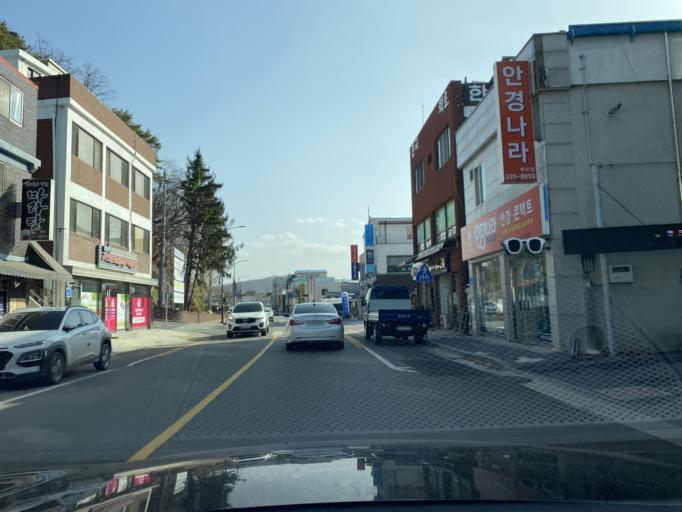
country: KR
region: Chungcheongnam-do
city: Yesan
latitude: 36.6792
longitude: 126.8378
